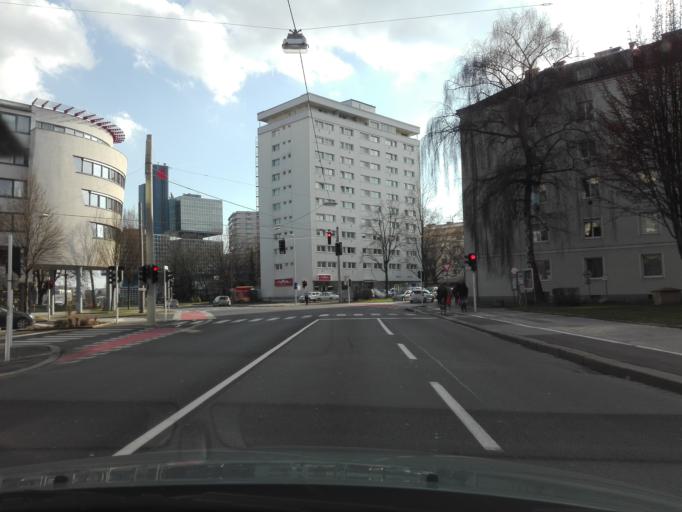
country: AT
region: Upper Austria
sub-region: Linz Stadt
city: Linz
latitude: 48.3180
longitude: 14.2832
